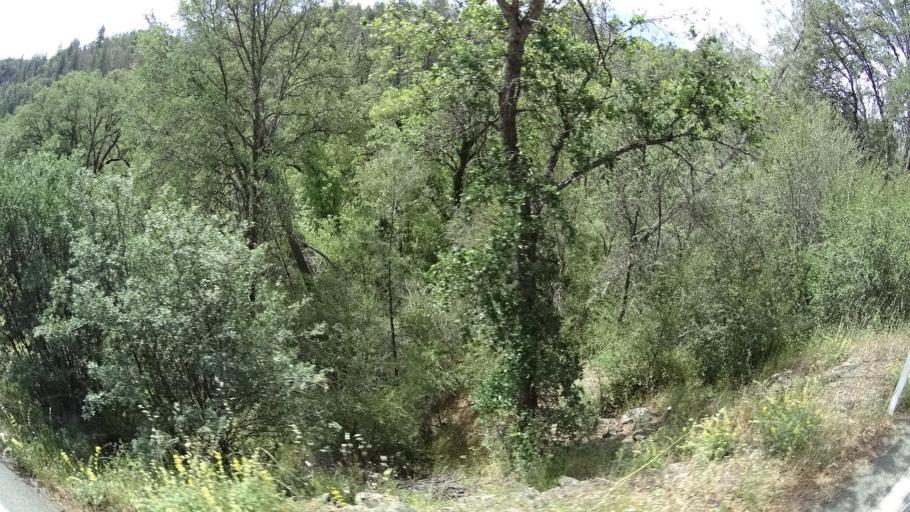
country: US
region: California
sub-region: Lake County
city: Lower Lake
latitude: 38.8836
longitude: -122.6685
